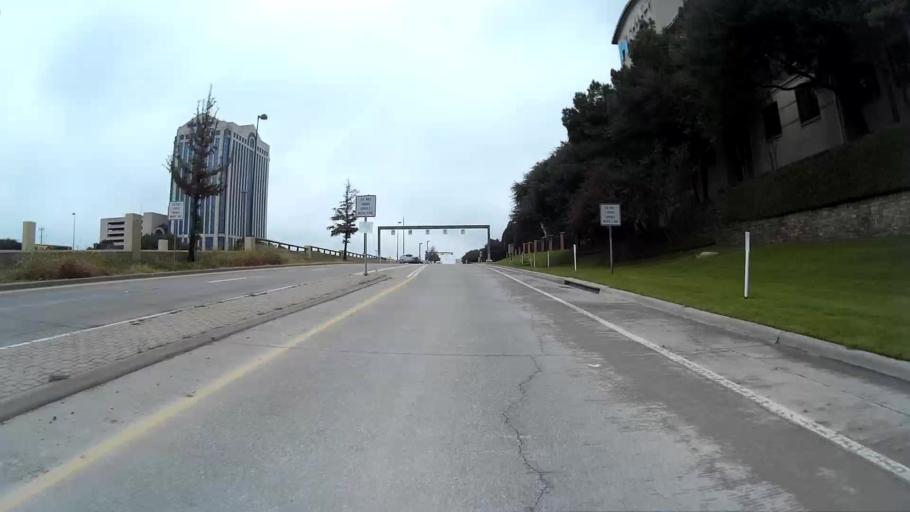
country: US
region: Texas
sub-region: Dallas County
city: University Park
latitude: 32.8624
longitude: -96.7708
